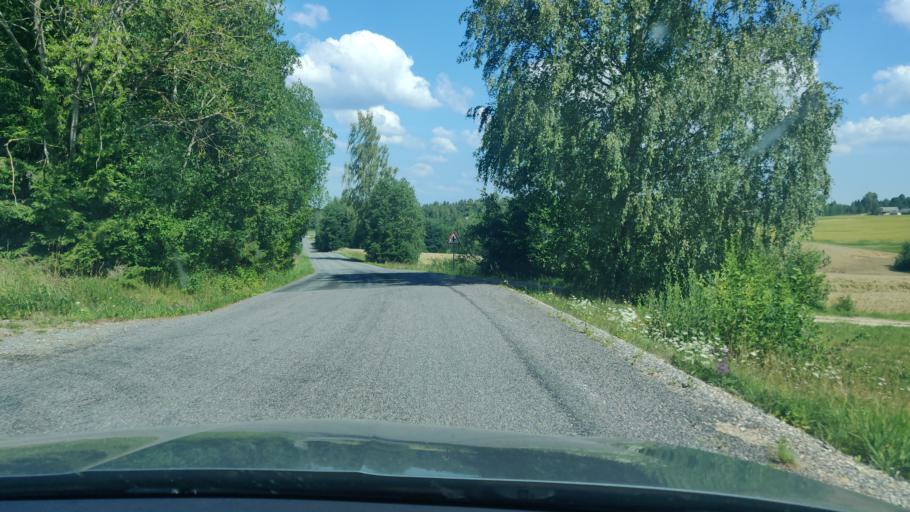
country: EE
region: Tartu
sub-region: Elva linn
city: Elva
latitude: 58.1402
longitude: 26.4775
